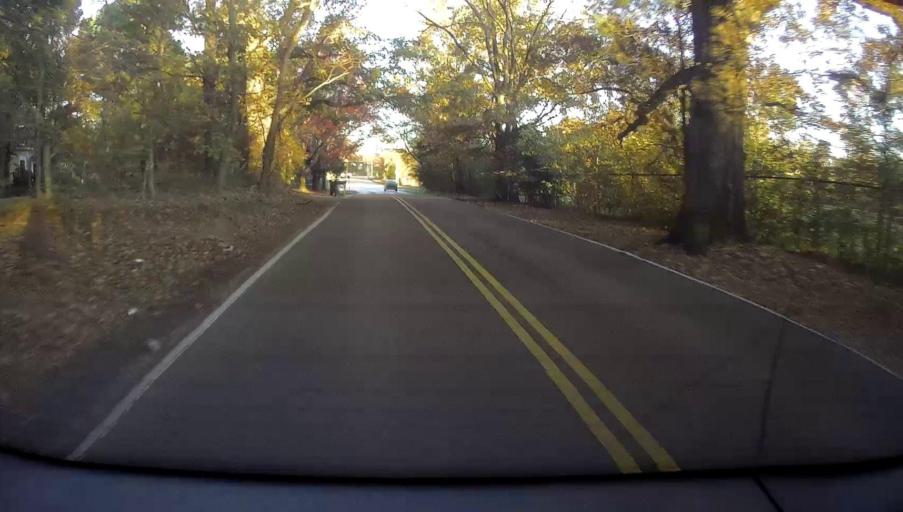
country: US
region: Tennessee
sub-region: Shelby County
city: Germantown
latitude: 35.0776
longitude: -89.8151
